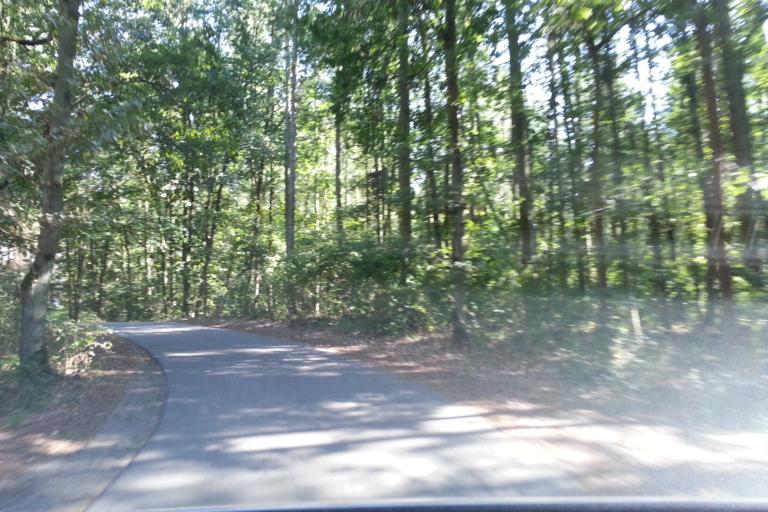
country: DE
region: Mecklenburg-Vorpommern
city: Torgelow
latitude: 53.6580
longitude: 14.0334
